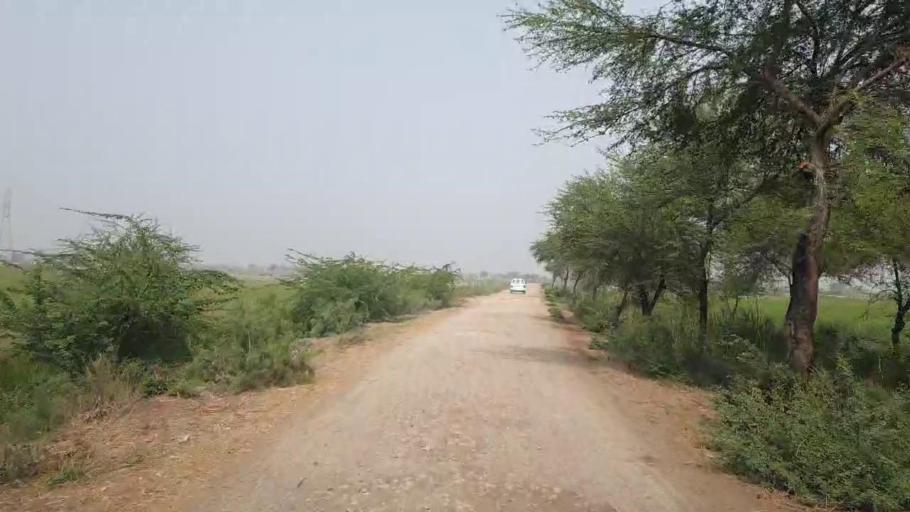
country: PK
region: Sindh
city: Kario
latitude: 24.6549
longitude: 68.6585
